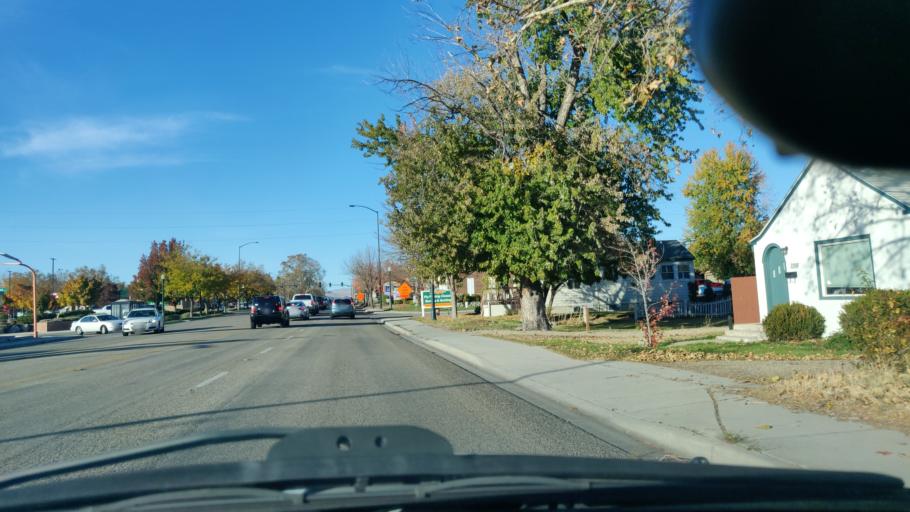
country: US
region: Idaho
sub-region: Ada County
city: Boise
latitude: 43.5880
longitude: -116.2136
